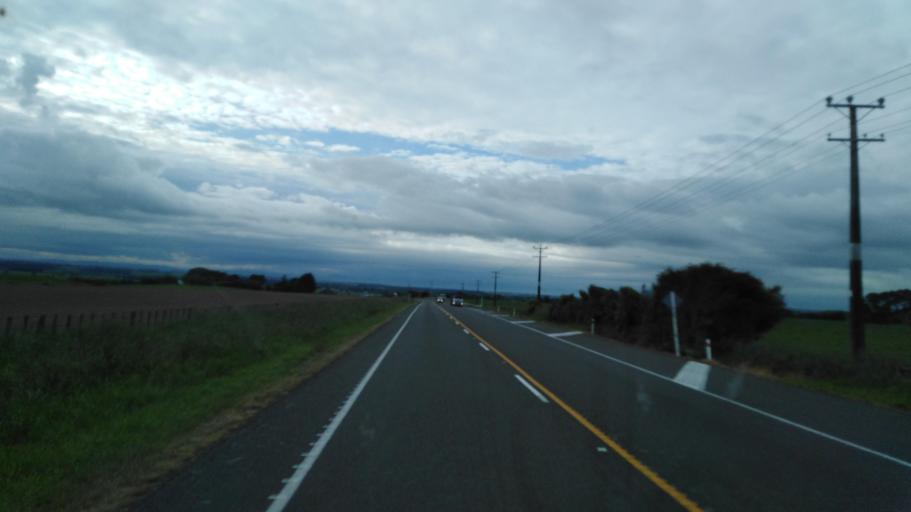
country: NZ
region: Manawatu-Wanganui
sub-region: Rangitikei District
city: Bulls
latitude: -40.1424
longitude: 175.3682
